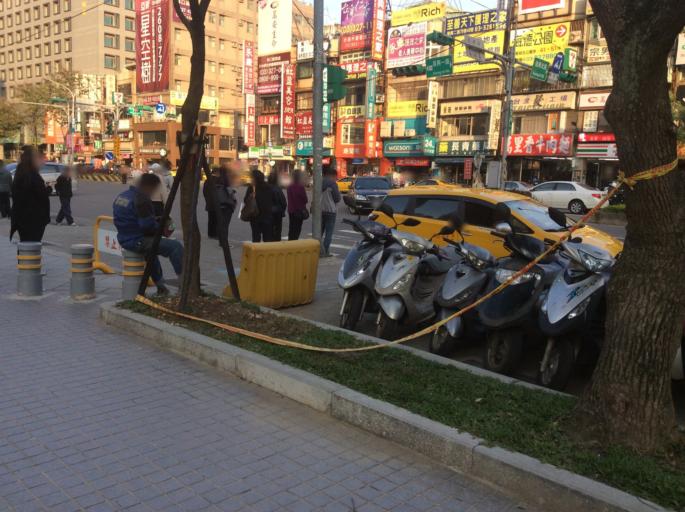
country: TW
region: Taiwan
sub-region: Taoyuan
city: Taoyuan
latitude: 25.0599
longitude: 121.3680
